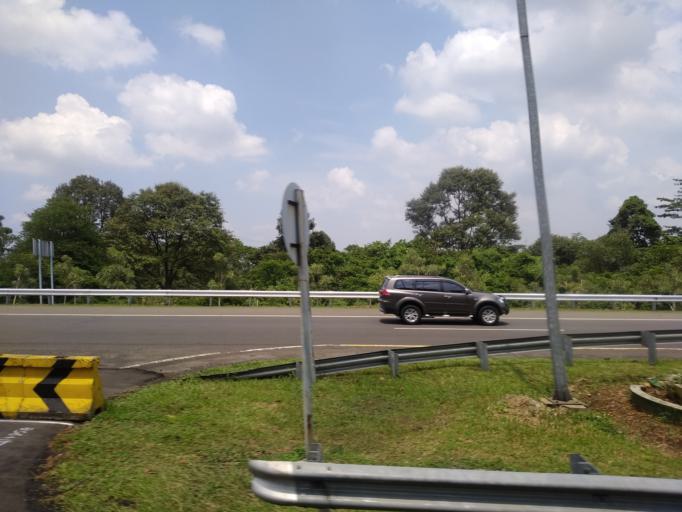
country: ID
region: West Java
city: Bogor
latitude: -6.5966
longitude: 106.8206
